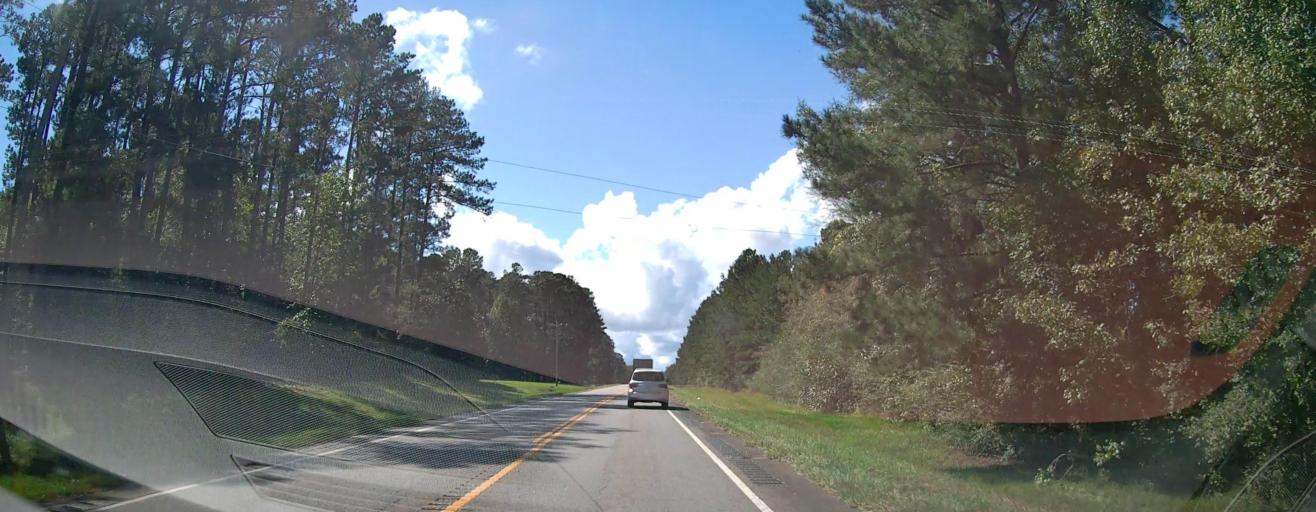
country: US
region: Georgia
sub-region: Jones County
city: Gray
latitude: 33.0388
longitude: -83.4050
